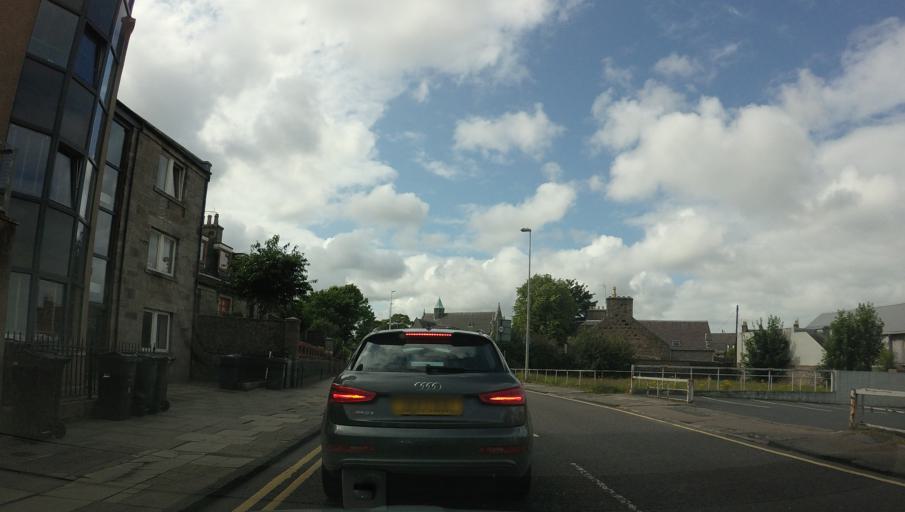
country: GB
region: Scotland
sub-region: Aberdeen City
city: Aberdeen
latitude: 57.1522
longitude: -2.1105
